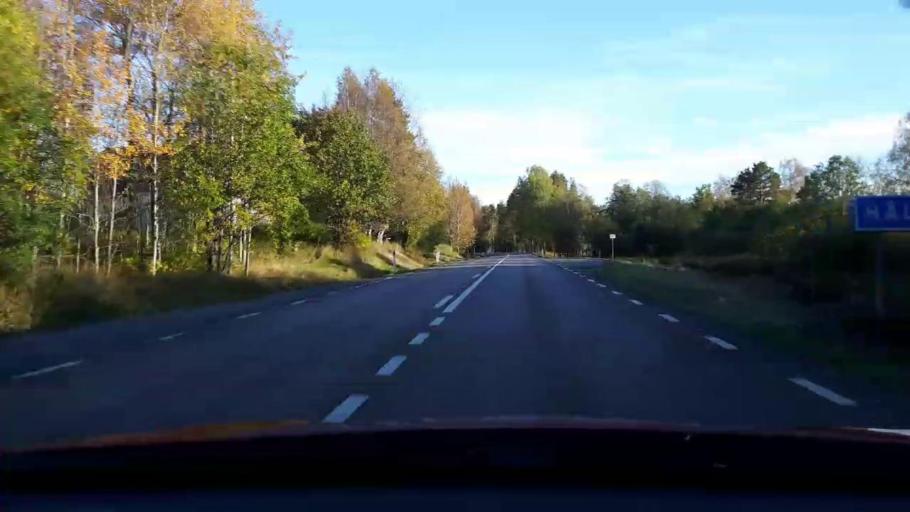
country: SE
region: Jaemtland
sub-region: OEstersunds Kommun
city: Brunflo
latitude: 63.0036
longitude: 14.9606
